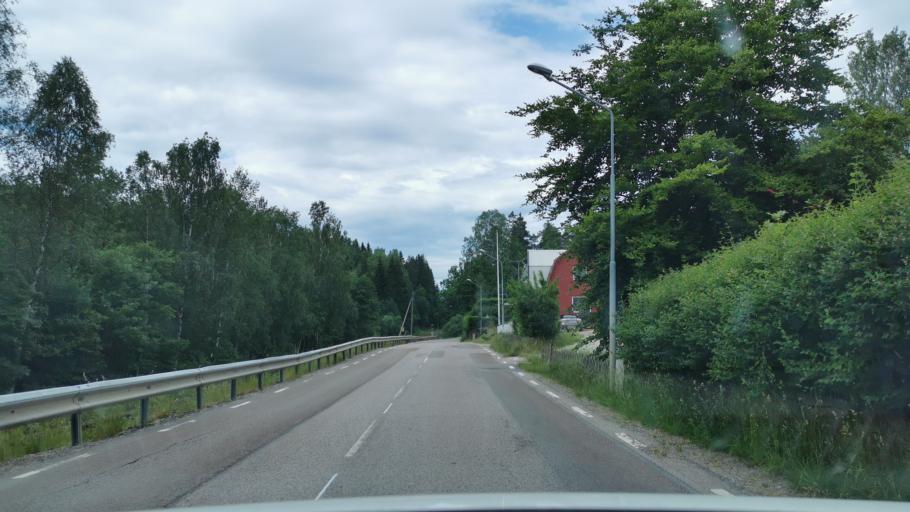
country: SE
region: Vaestra Goetaland
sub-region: Melleruds Kommun
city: Mellerud
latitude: 58.8274
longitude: 12.4132
